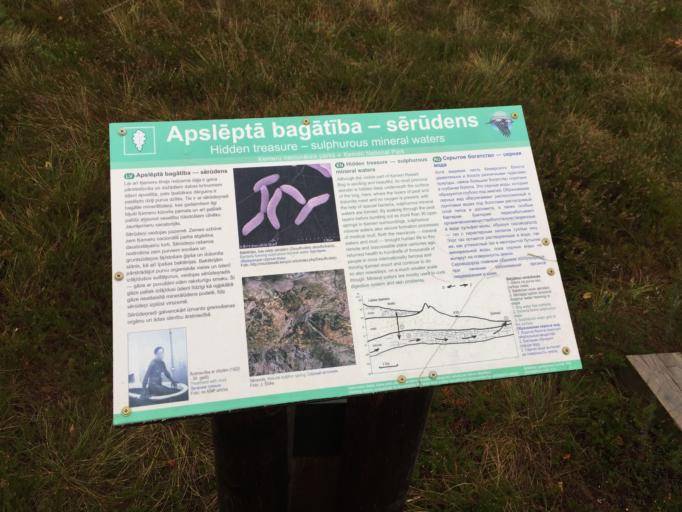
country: LV
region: Engure
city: Smarde
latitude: 56.9079
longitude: 23.4586
